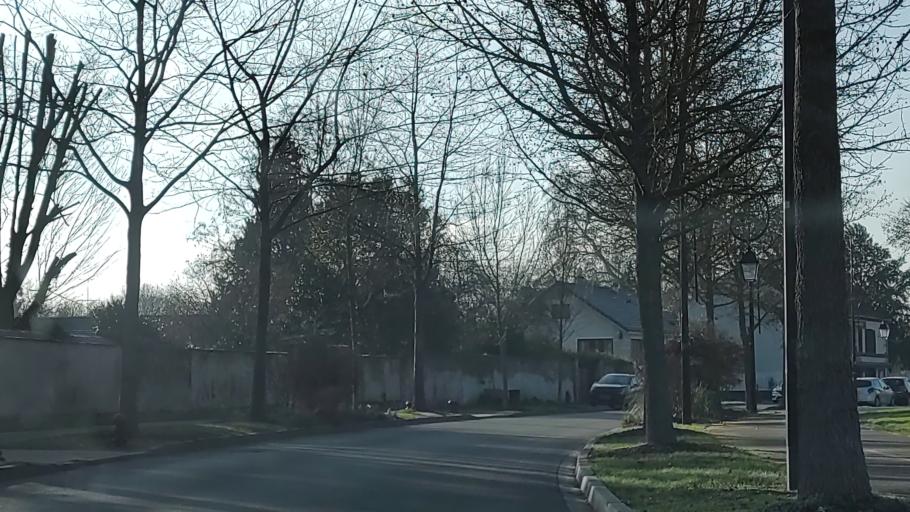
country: FR
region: Ile-de-France
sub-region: Departement de Seine-et-Marne
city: Claye-Souilly
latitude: 48.9448
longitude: 2.6980
